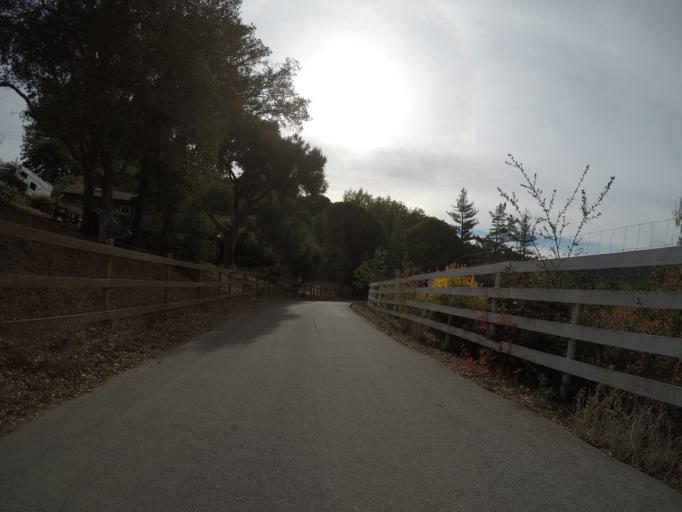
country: US
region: California
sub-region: Santa Cruz County
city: Scotts Valley
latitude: 37.0567
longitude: -121.9915
